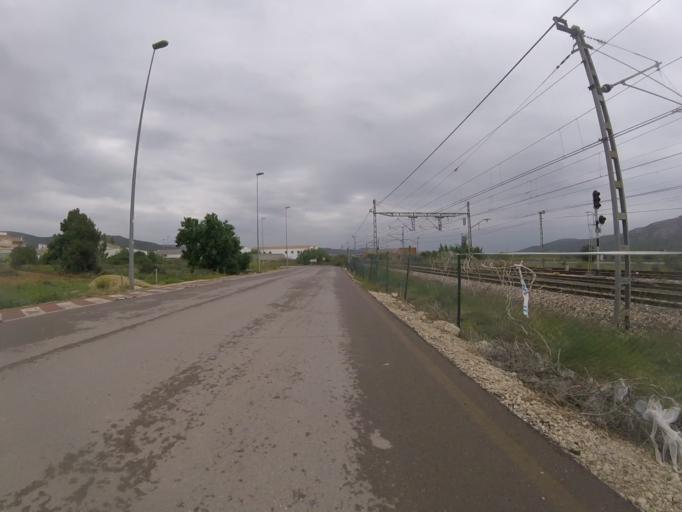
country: ES
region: Valencia
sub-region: Provincia de Castello
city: Alcala de Xivert
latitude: 40.3072
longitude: 0.2298
